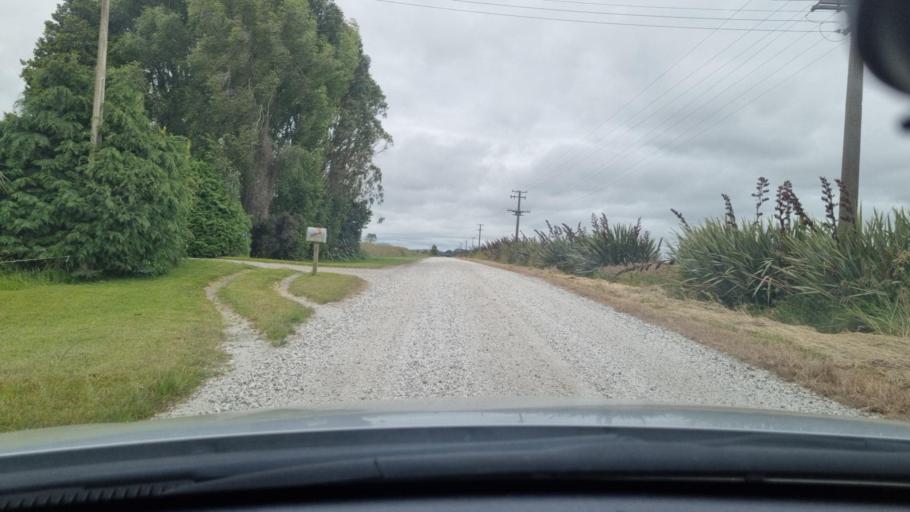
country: NZ
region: Southland
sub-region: Invercargill City
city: Invercargill
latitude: -46.3864
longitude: 168.2814
